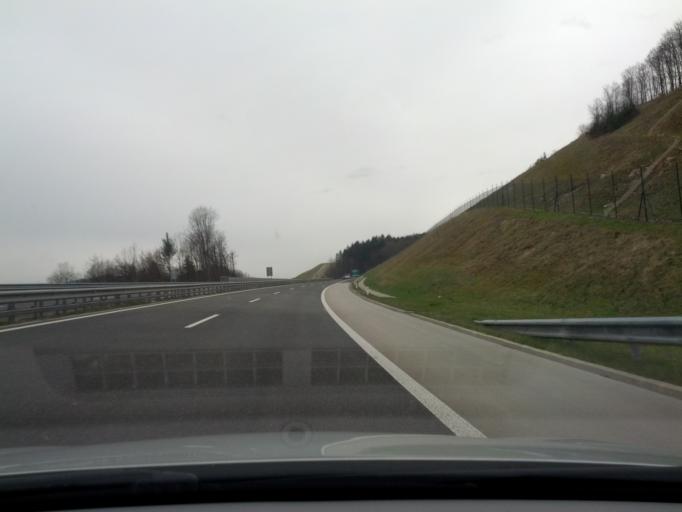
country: SI
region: Trebnje
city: Trebnje
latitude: 45.9023
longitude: 15.0068
